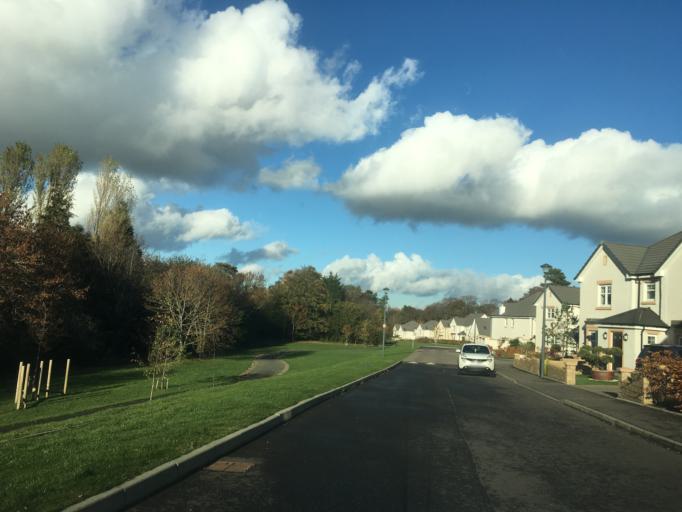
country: GB
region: Scotland
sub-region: Edinburgh
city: Colinton
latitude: 55.9000
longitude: -3.2503
